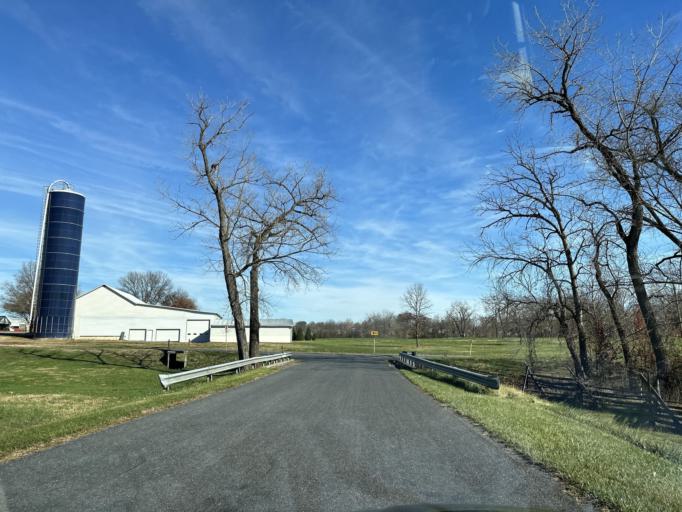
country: US
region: Virginia
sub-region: Rockingham County
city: Bridgewater
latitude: 38.3506
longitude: -78.9495
